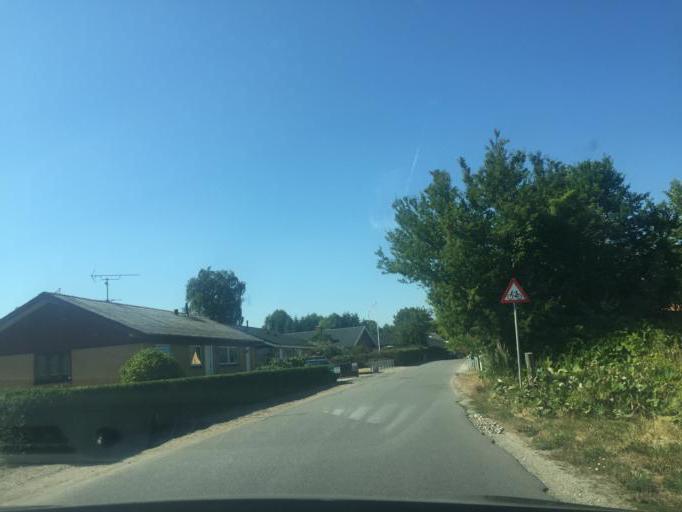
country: DK
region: Central Jutland
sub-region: Hedensted Kommune
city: Juelsminde
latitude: 55.7101
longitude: 9.9762
